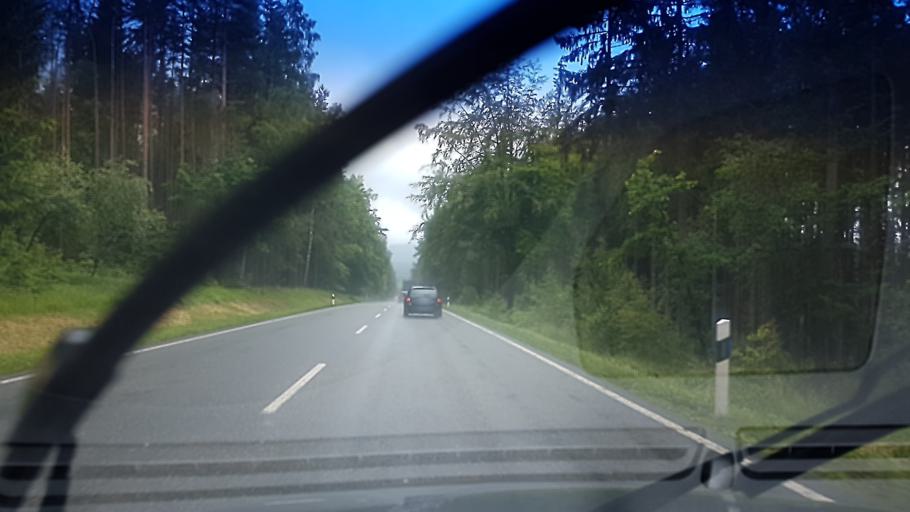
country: DE
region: Bavaria
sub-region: Upper Franconia
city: Wunsiedel
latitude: 50.0165
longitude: 11.9820
